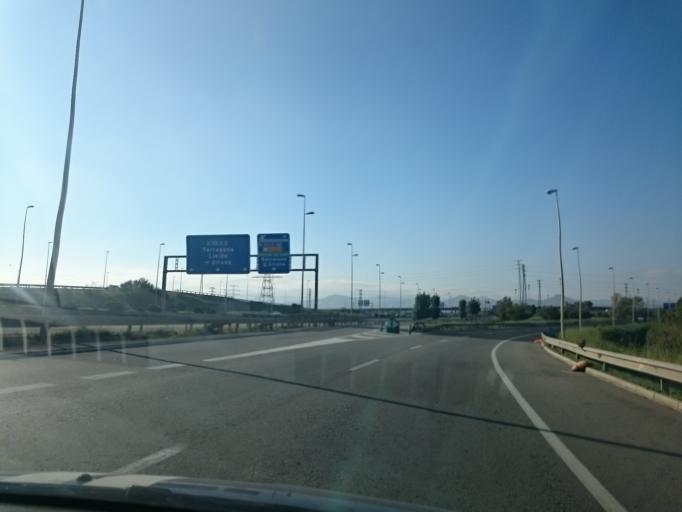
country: ES
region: Catalonia
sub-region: Provincia de Barcelona
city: El Prat de Llobregat
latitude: 41.3412
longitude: 2.1001
